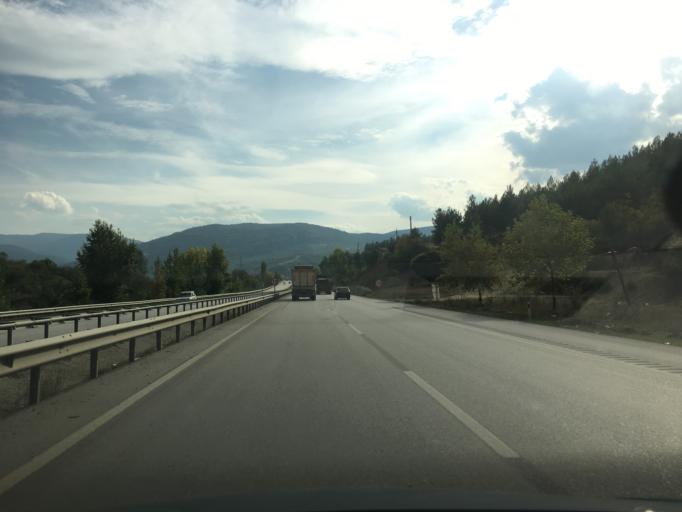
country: TR
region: Karabuk
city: Karabuk
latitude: 41.1165
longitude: 32.6723
